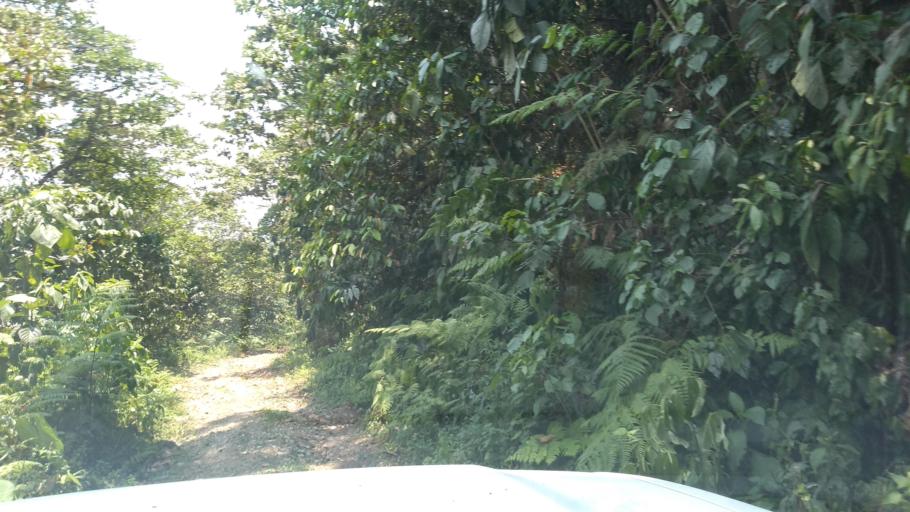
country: MX
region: Veracruz
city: Motzorongo
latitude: 18.6058
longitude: -96.7581
